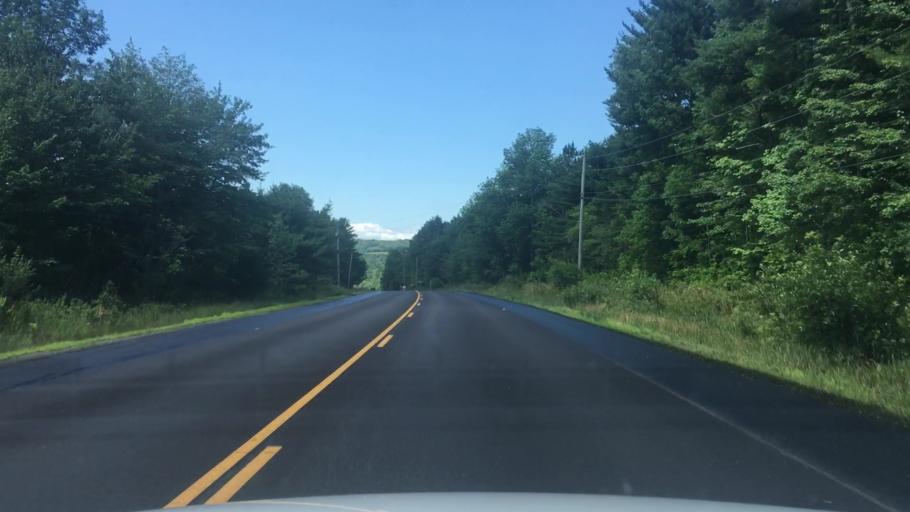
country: US
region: Maine
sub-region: Waldo County
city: Searsmont
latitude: 44.4025
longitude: -69.2713
